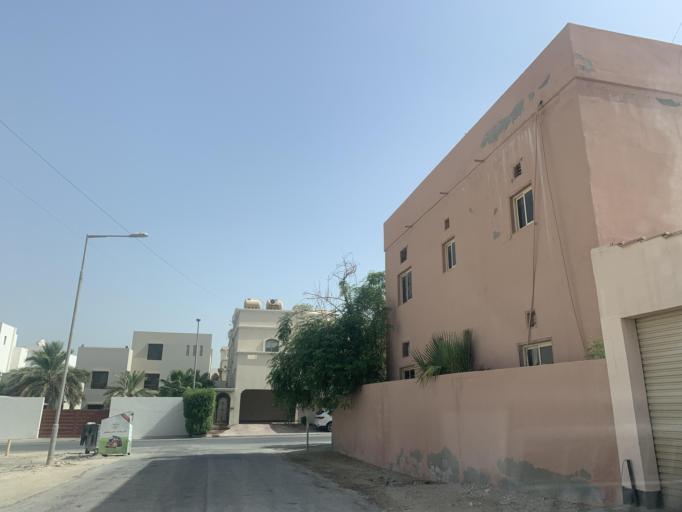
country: BH
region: Northern
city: Madinat `Isa
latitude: 26.1531
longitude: 50.5324
